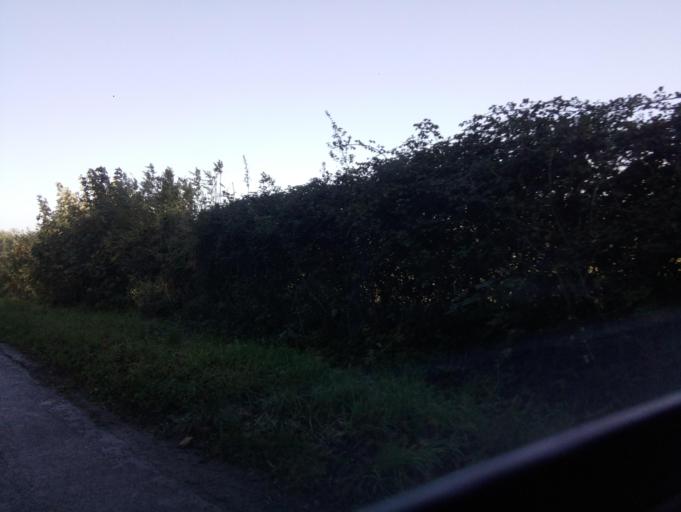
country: GB
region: England
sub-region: Somerset
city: Castle Cary
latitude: 51.0269
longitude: -2.4993
